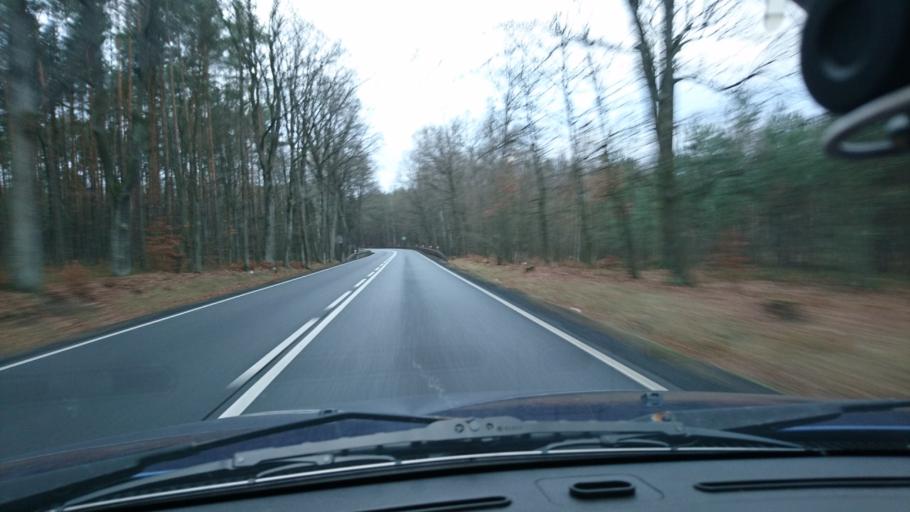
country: PL
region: Opole Voivodeship
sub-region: Powiat oleski
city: Olesno
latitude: 50.9356
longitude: 18.3309
